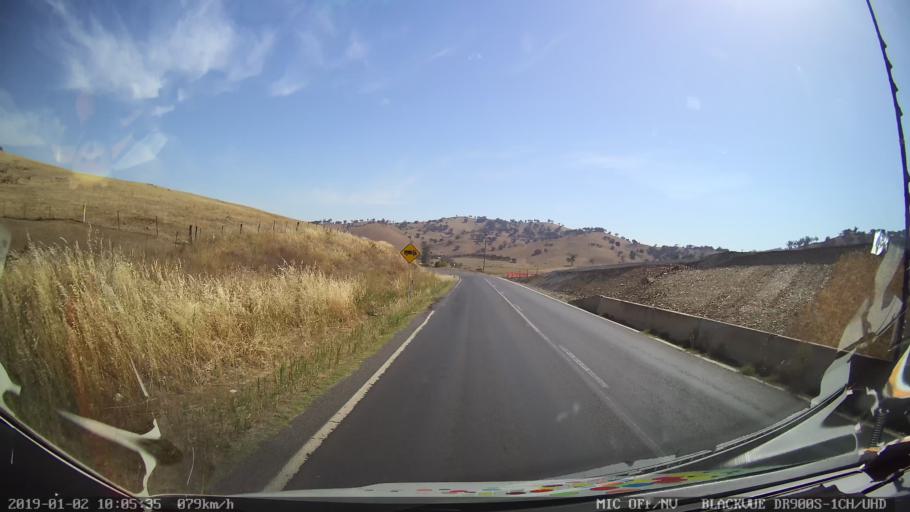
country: AU
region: New South Wales
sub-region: Gundagai
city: Gundagai
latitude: -35.1579
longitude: 148.1179
